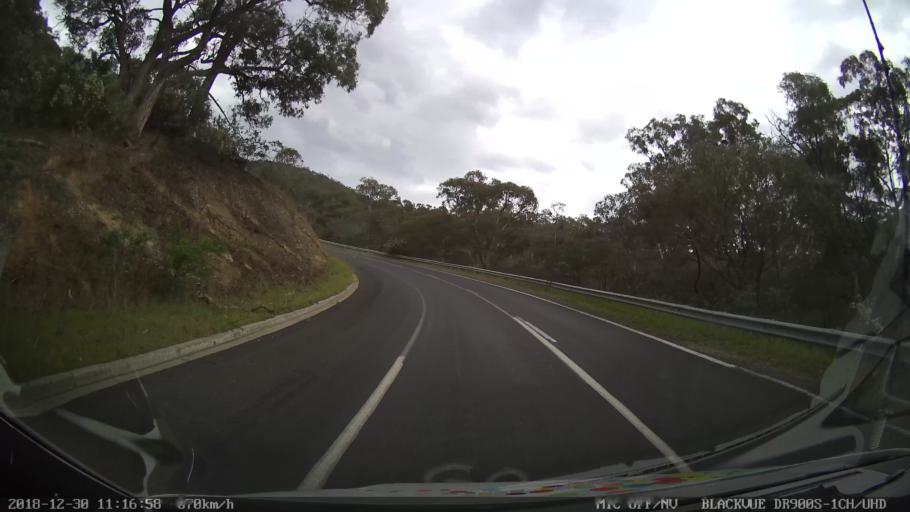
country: AU
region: New South Wales
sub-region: Snowy River
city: Jindabyne
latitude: -36.5372
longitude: 148.7022
